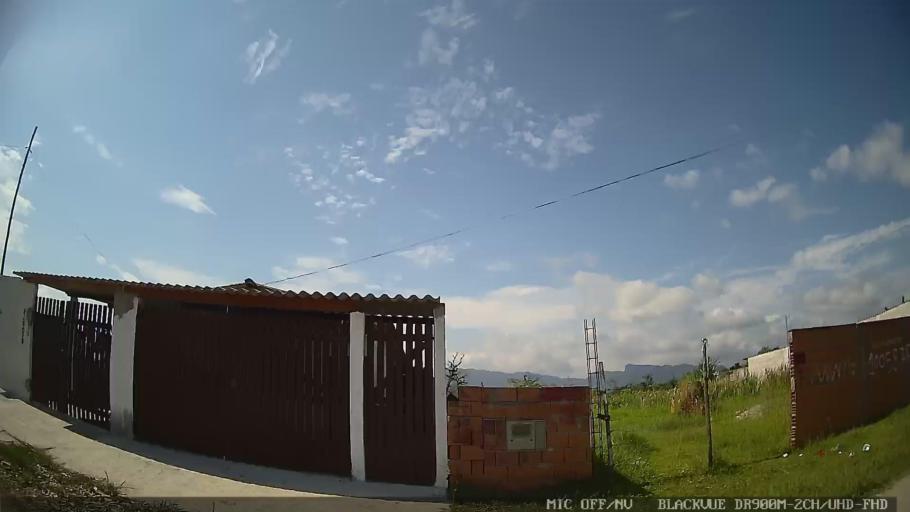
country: BR
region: Sao Paulo
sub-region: Caraguatatuba
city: Caraguatatuba
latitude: -23.6728
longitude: -45.4595
